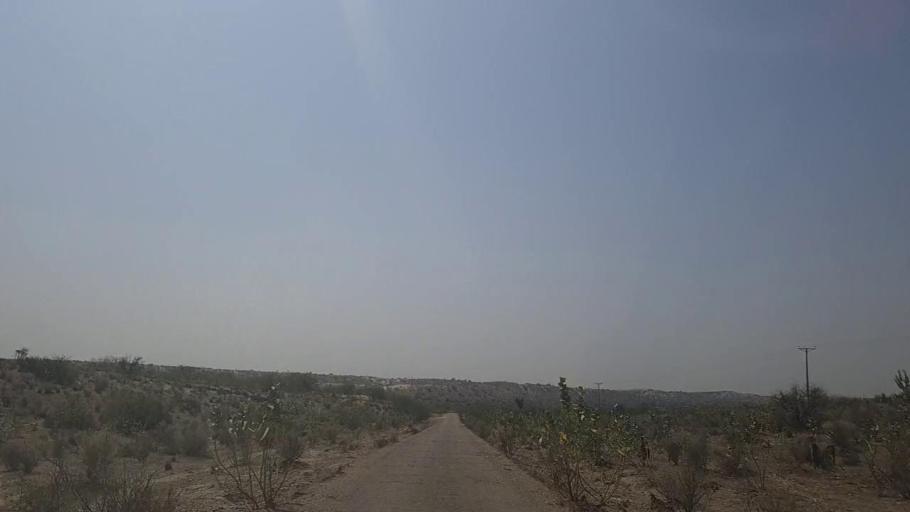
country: PK
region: Sindh
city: Naukot
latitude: 24.8246
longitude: 69.4828
